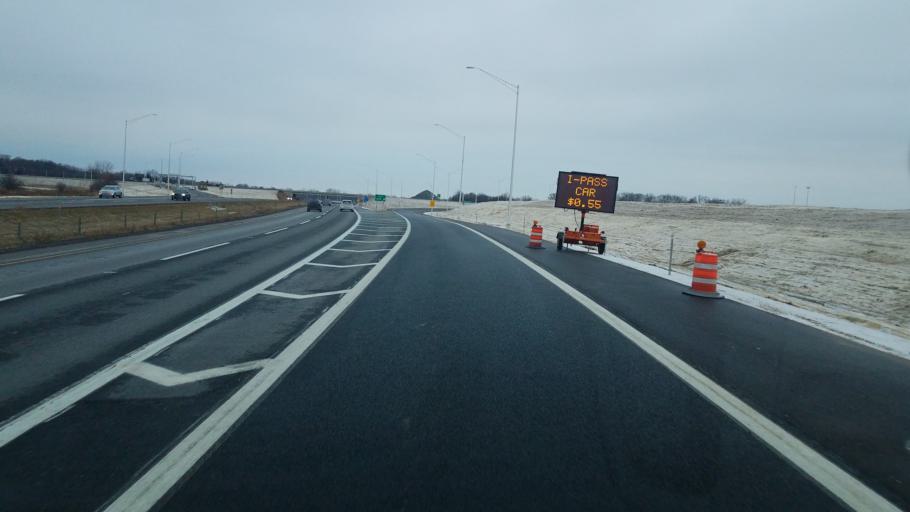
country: US
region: Illinois
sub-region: Kane County
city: Sugar Grove
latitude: 41.8180
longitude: -88.4601
